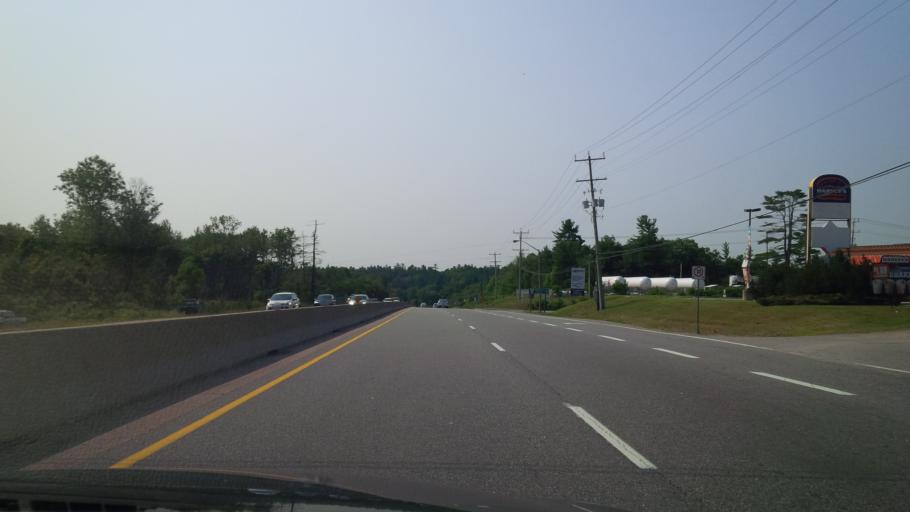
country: CA
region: Ontario
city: Gravenhurst
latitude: 44.8660
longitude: -79.3243
